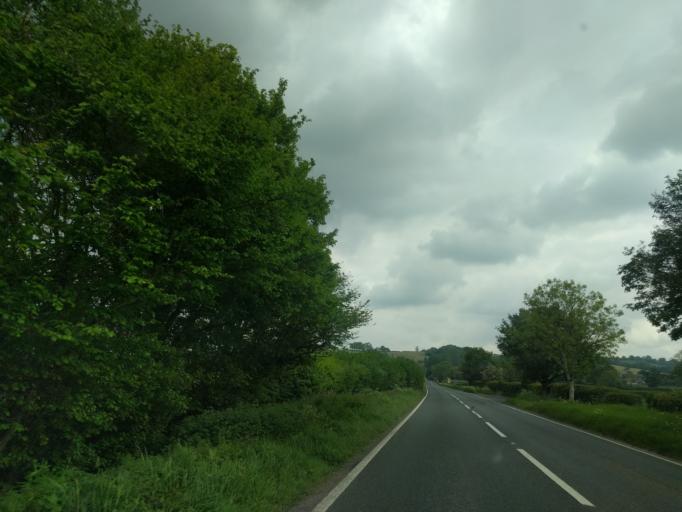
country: GB
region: England
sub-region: Somerset
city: Castle Cary
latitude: 51.1202
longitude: -2.5769
